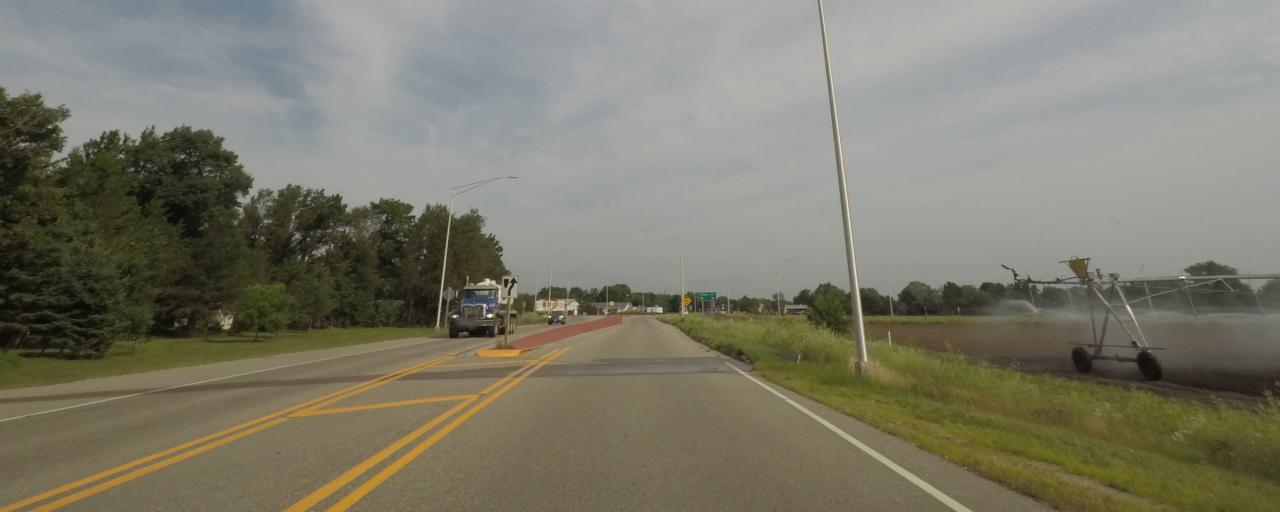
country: US
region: Wisconsin
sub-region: Portage County
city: Plover
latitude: 44.4486
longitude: -89.5431
